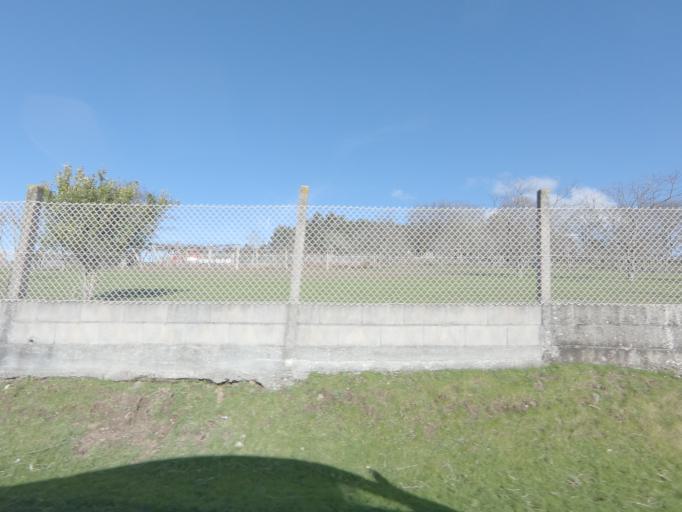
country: ES
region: Galicia
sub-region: Provincia da Coruna
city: Ribeira
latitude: 42.7060
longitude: -8.4285
